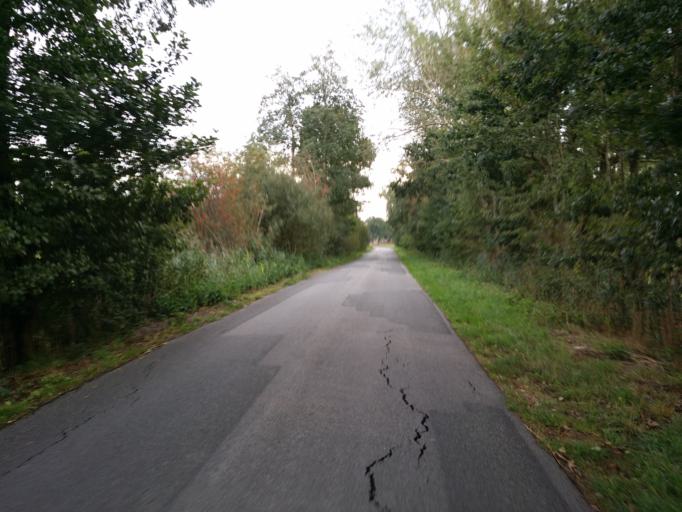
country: DE
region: Lower Saxony
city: Hollnseth
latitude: 53.5715
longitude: 9.1197
